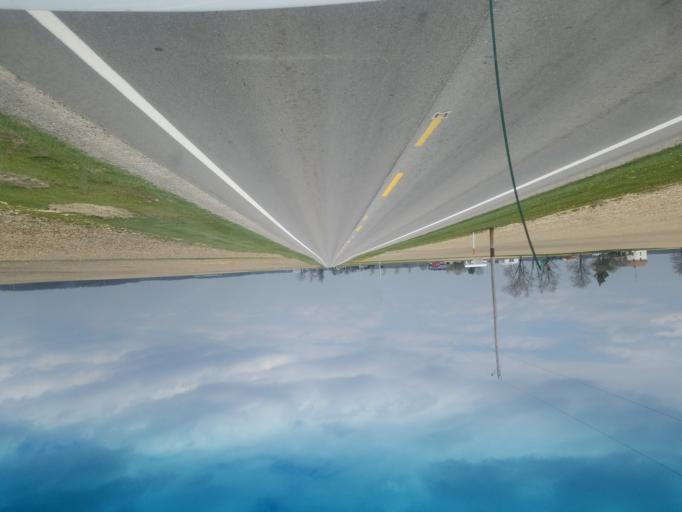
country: US
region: Ohio
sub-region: Wyandot County
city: Upper Sandusky
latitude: 40.9083
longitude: -83.2747
